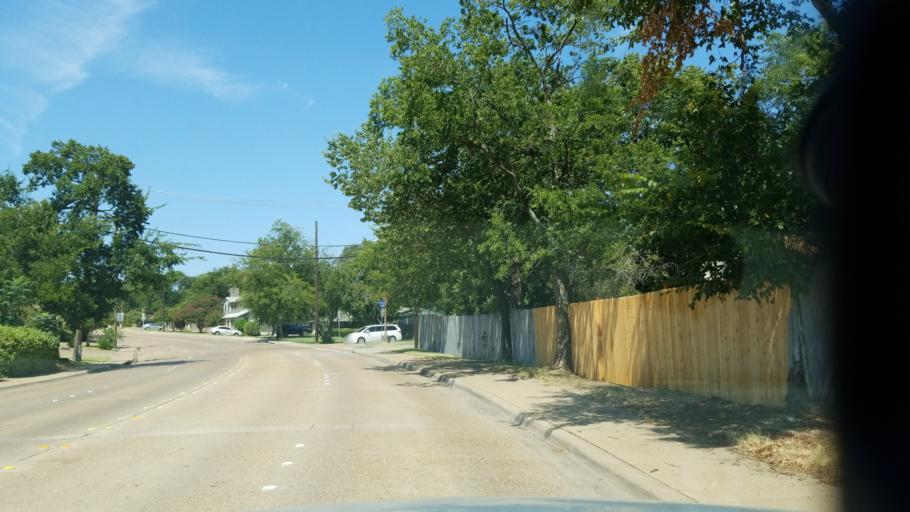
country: US
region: Texas
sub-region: Dallas County
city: Duncanville
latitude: 32.6515
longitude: -96.9016
